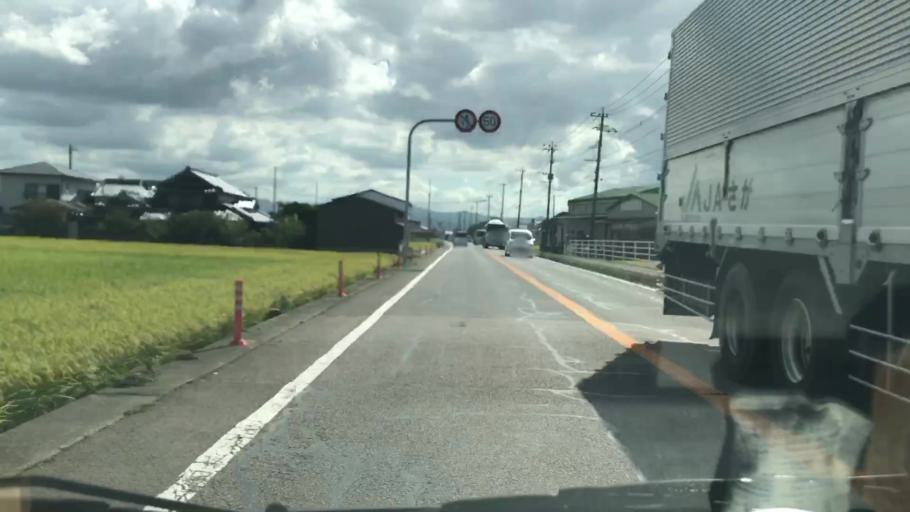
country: JP
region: Saga Prefecture
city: Kashima
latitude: 33.1770
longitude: 130.1848
